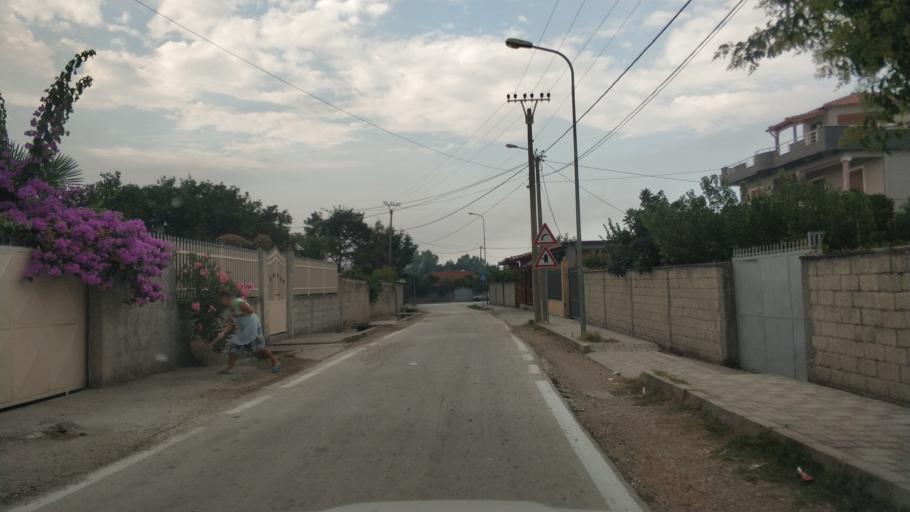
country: AL
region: Fier
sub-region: Rrethi i Fierit
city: Dermenas
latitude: 40.7292
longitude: 19.4684
